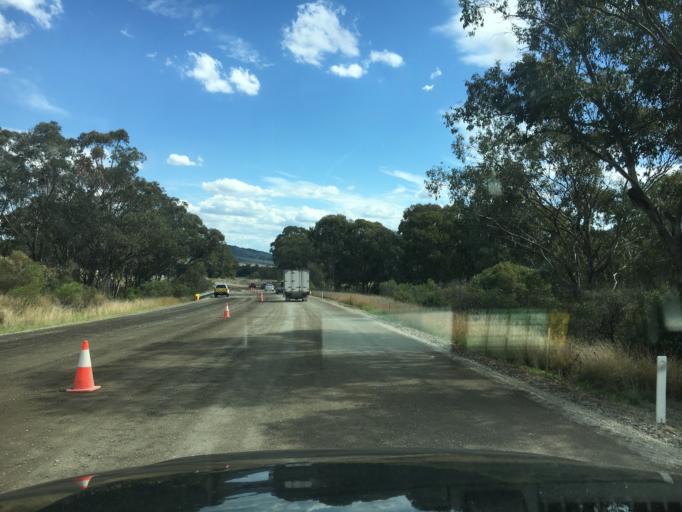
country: AU
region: New South Wales
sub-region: Liverpool Plains
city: Quirindi
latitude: -31.4518
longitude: 150.8627
